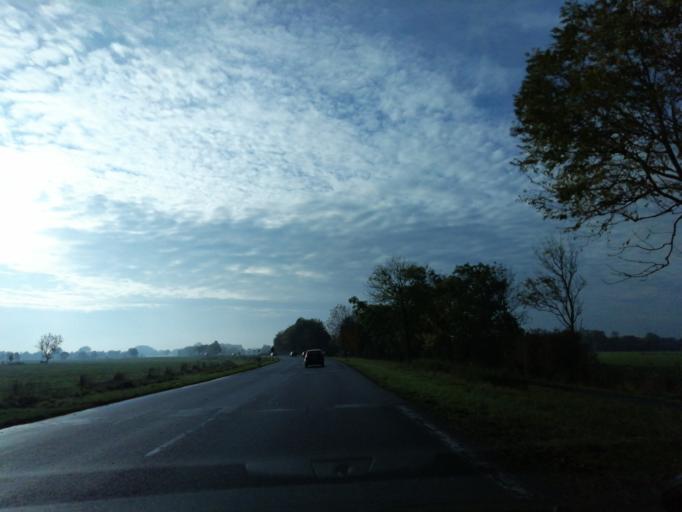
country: DE
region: Lower Saxony
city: Fedderwarden
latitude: 53.6057
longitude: 8.0455
